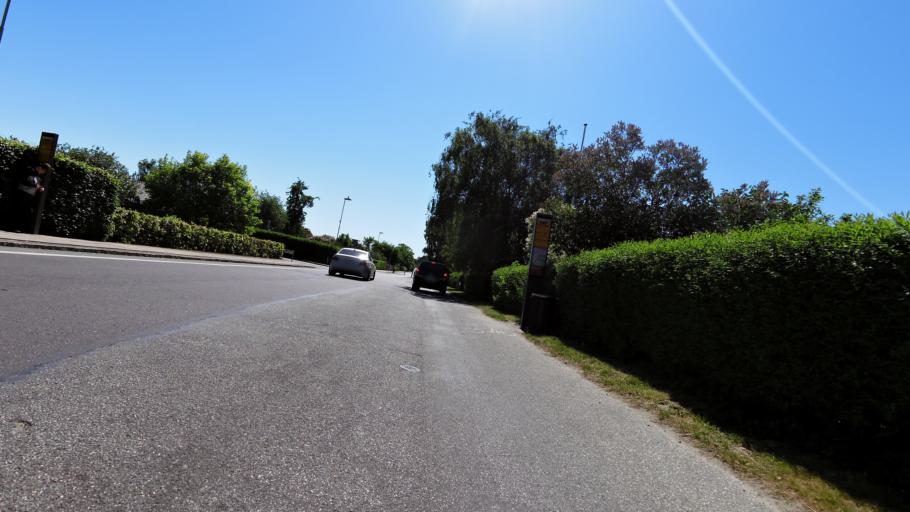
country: DK
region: Central Jutland
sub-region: Arhus Kommune
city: Framlev
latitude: 56.1510
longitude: 10.0044
